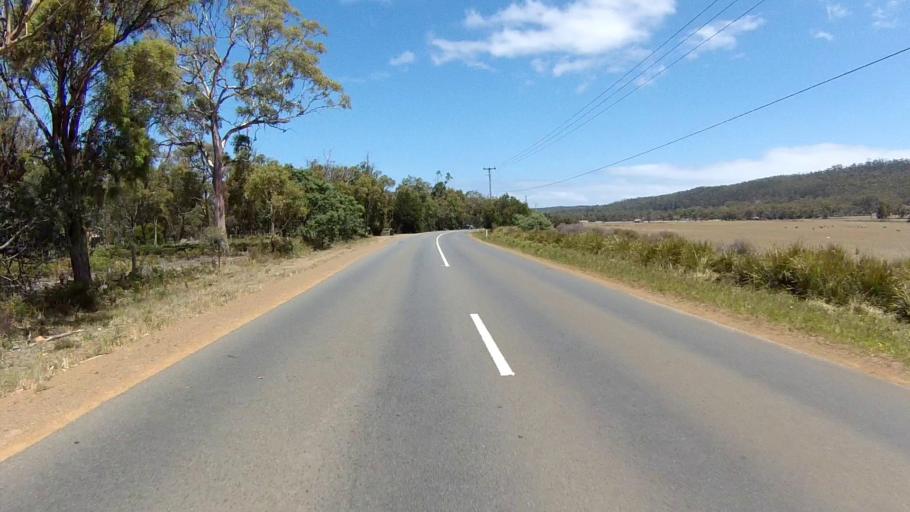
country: AU
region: Tasmania
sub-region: Clarence
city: Sandford
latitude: -42.9405
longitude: 147.4883
